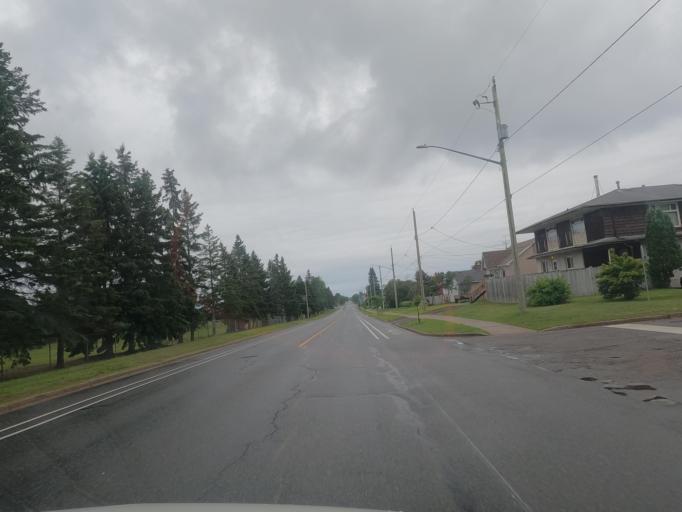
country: CA
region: Ontario
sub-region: Thunder Bay District
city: Thunder Bay
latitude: 48.4726
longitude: -89.1824
